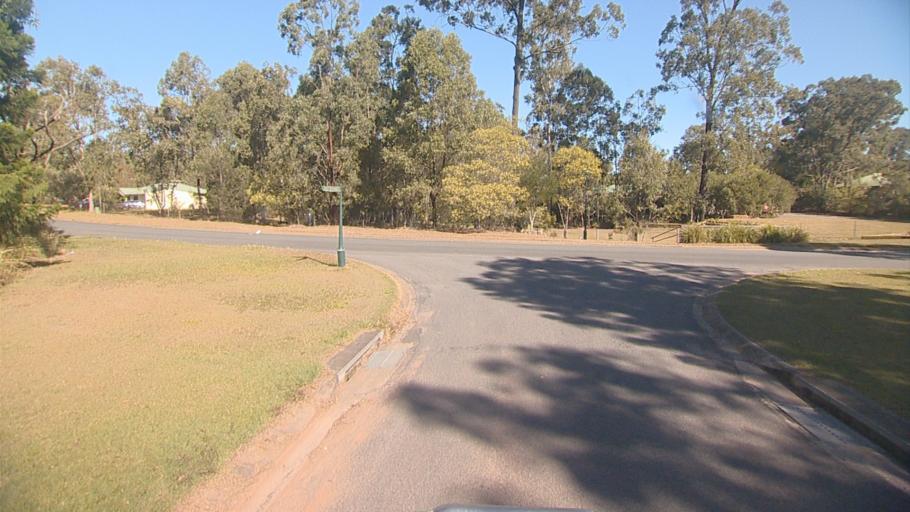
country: AU
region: Queensland
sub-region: Logan
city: North Maclean
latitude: -27.8202
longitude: 152.9533
